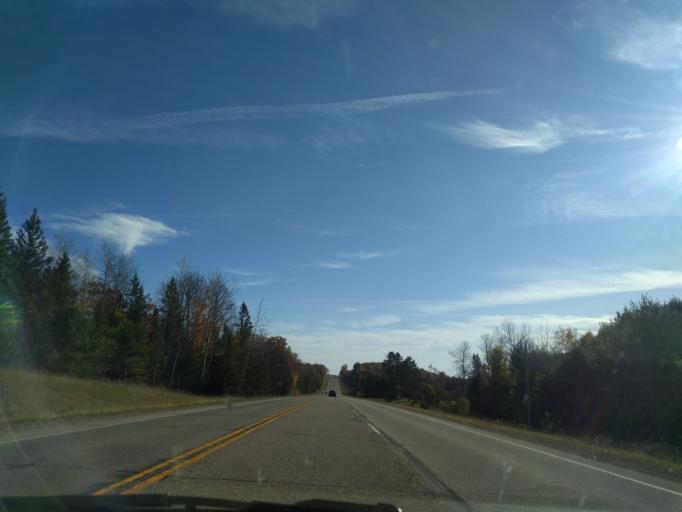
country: US
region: Wisconsin
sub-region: Marinette County
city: Niagara
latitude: 45.4834
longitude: -87.9865
